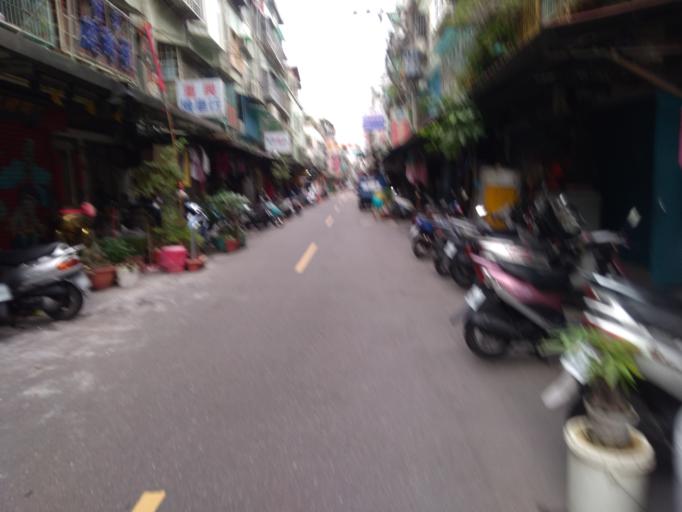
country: TW
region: Taipei
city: Taipei
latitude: 25.0843
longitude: 121.4921
